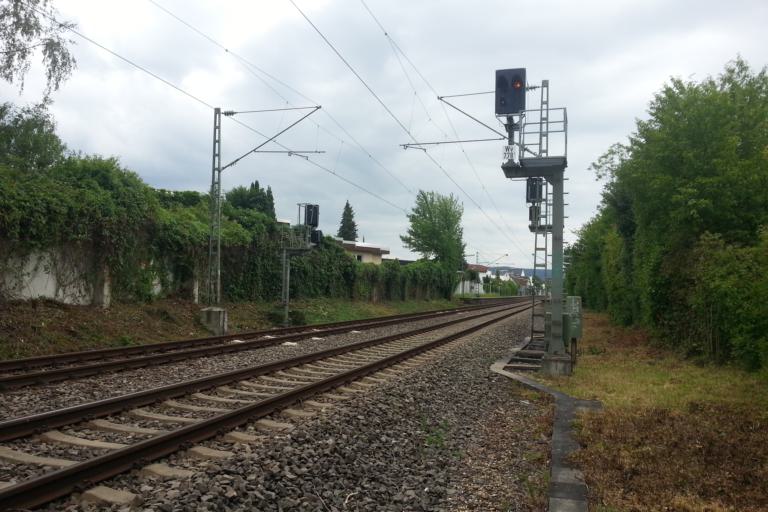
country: DE
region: Baden-Wuerttemberg
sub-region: Regierungsbezirk Stuttgart
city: Weinstadt-Endersbach
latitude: 48.8127
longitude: 9.3558
